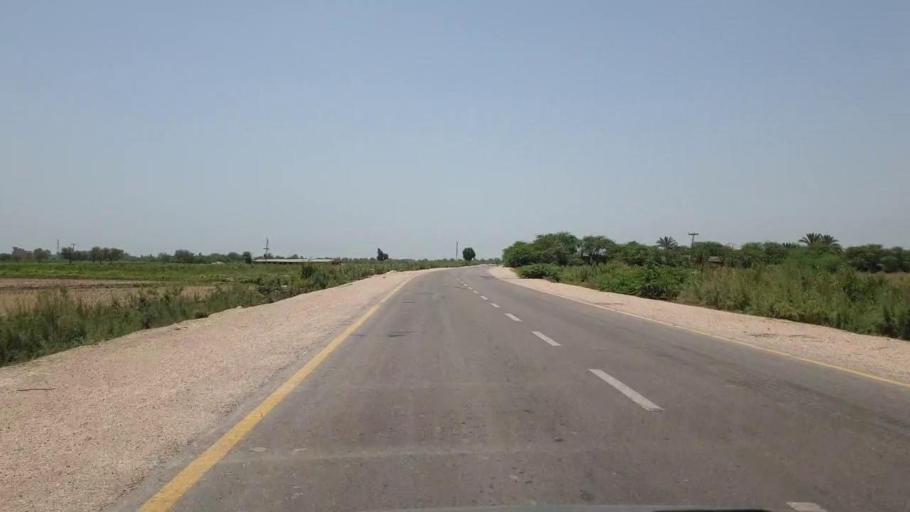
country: PK
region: Sindh
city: Sakrand
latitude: 26.1240
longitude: 68.3821
